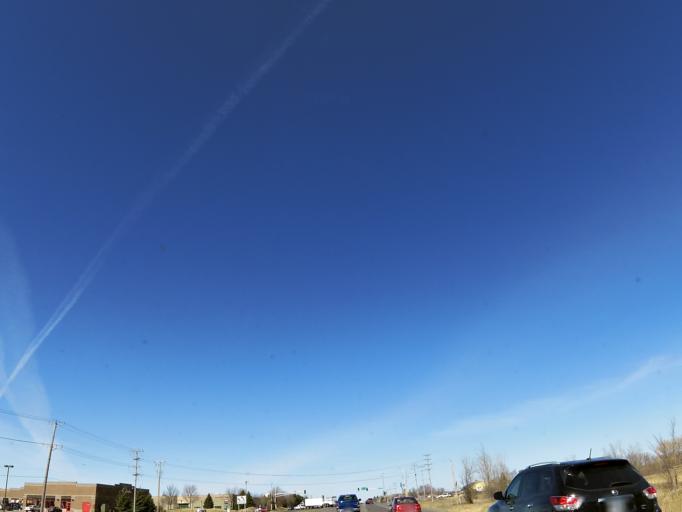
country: US
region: Minnesota
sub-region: Hennepin County
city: Plymouth
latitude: 45.0208
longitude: -93.4908
